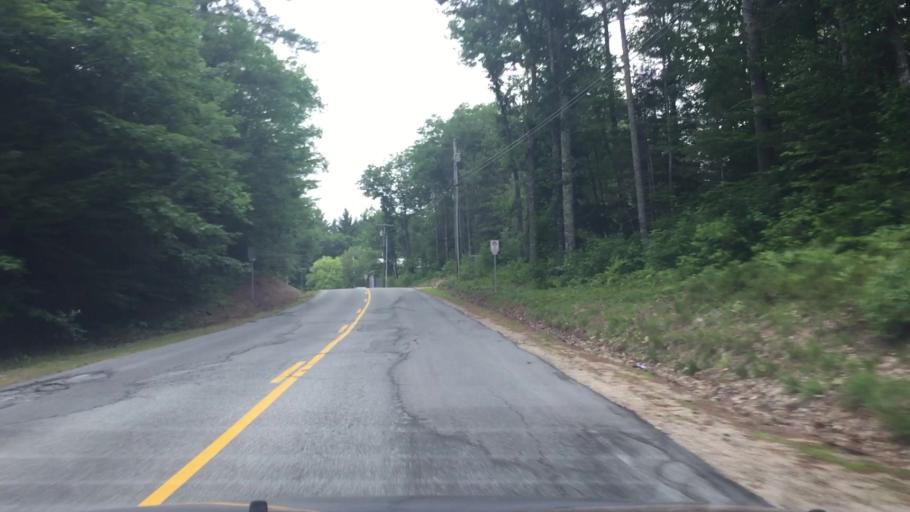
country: US
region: New Hampshire
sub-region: Carroll County
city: North Conway
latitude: 44.0792
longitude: -71.1637
